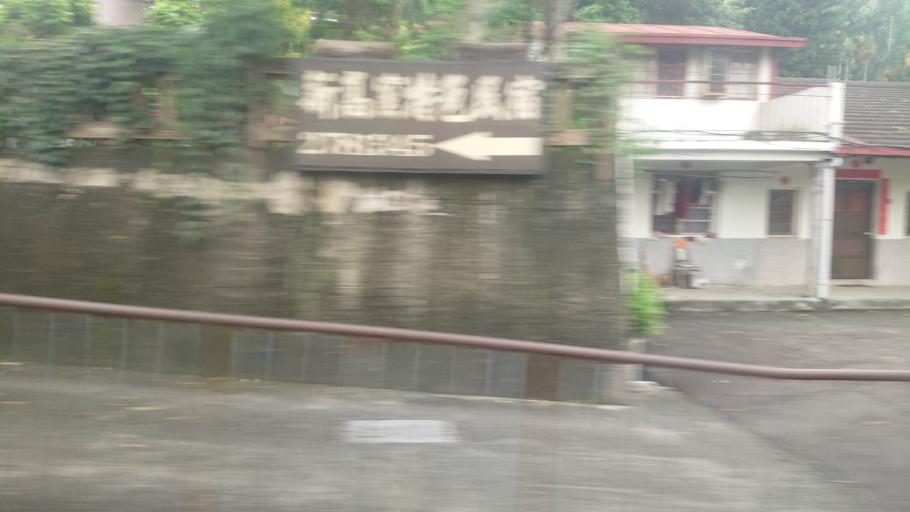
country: TW
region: Taiwan
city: Lugu
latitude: 23.8345
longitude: 120.7515
